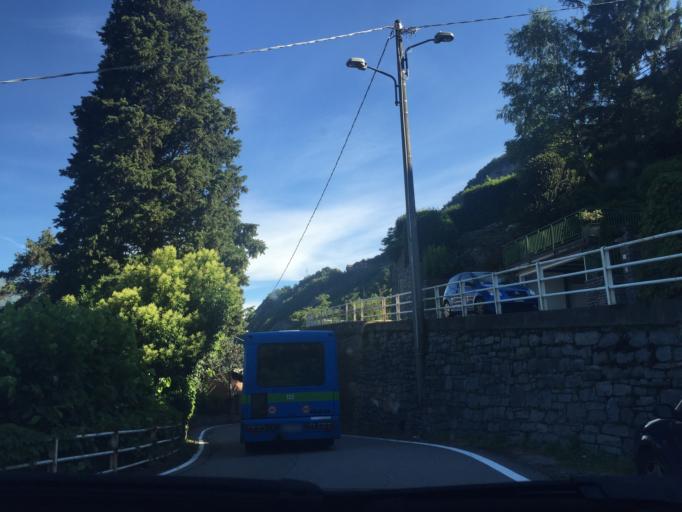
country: IT
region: Lombardy
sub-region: Provincia di Lecco
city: Varenna
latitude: 46.0149
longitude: 9.2875
